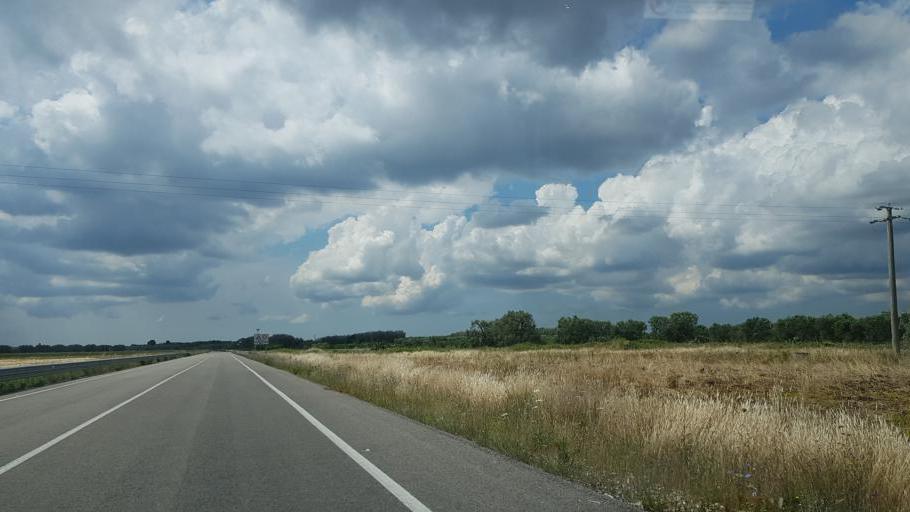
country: IT
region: Apulia
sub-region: Provincia di Brindisi
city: Mesagne
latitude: 40.5017
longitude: 17.8283
